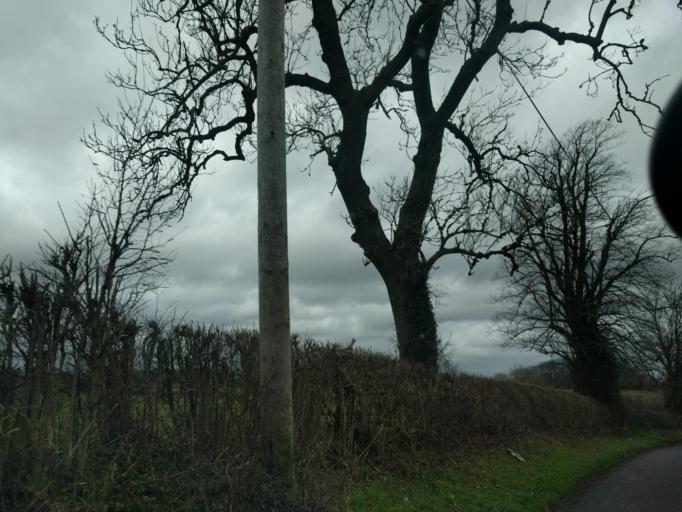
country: GB
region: England
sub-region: Wiltshire
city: Biddestone
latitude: 51.5041
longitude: -2.1987
